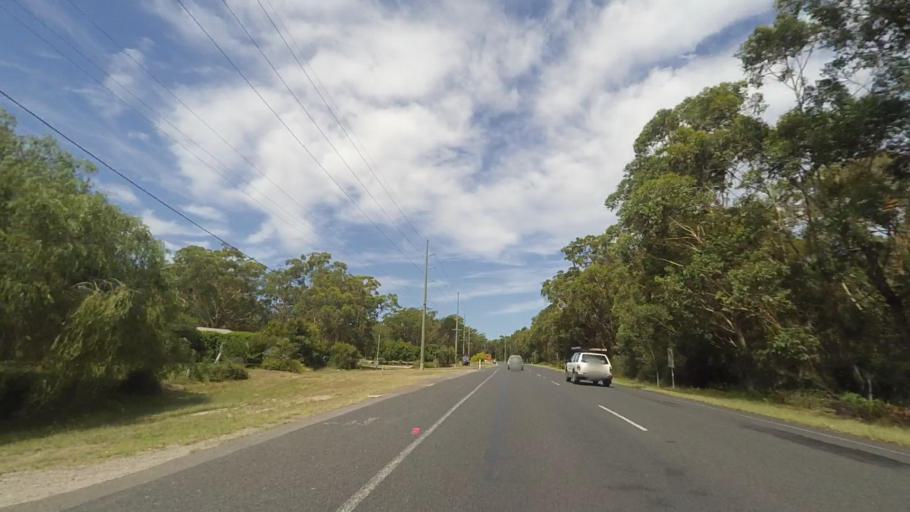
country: AU
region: New South Wales
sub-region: Port Stephens Shire
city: Anna Bay
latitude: -32.7842
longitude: 151.9759
